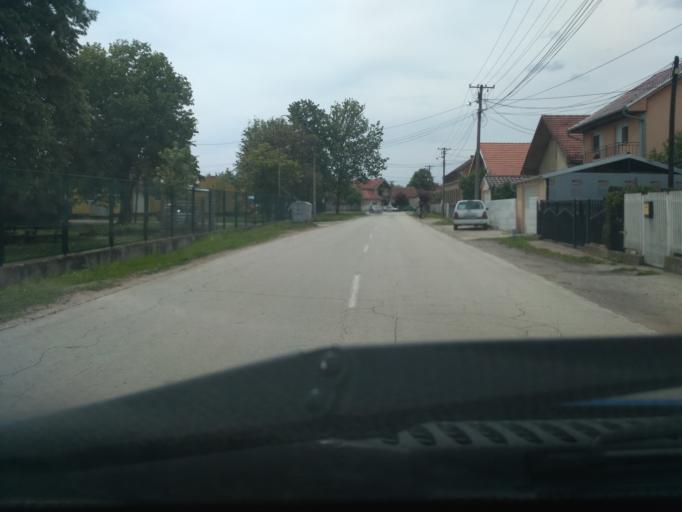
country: RS
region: Central Serbia
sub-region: Pomoravski Okrug
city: Svilajnac
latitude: 44.2341
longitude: 21.2028
